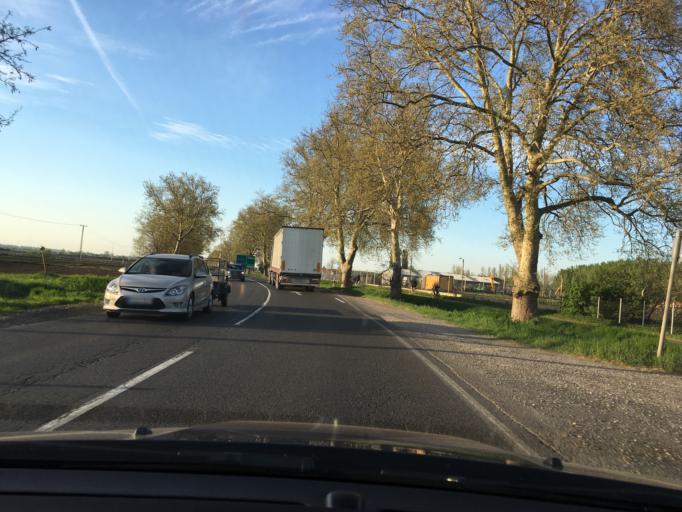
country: HU
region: Hajdu-Bihar
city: Mikepercs
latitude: 47.4585
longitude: 21.6366
